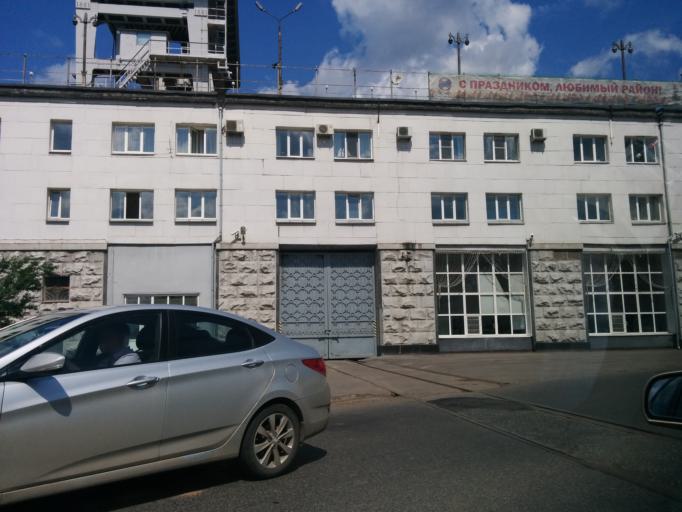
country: RU
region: Perm
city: Perm
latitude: 58.1140
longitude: 56.3245
